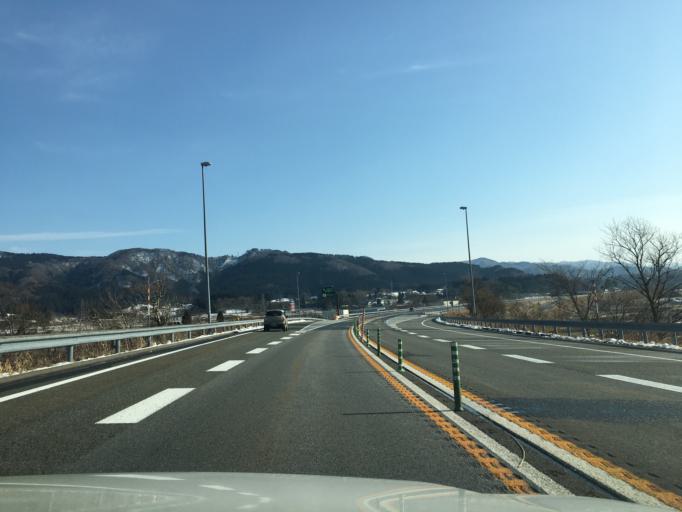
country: JP
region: Yamagata
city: Tsuruoka
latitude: 38.6218
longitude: 139.8432
